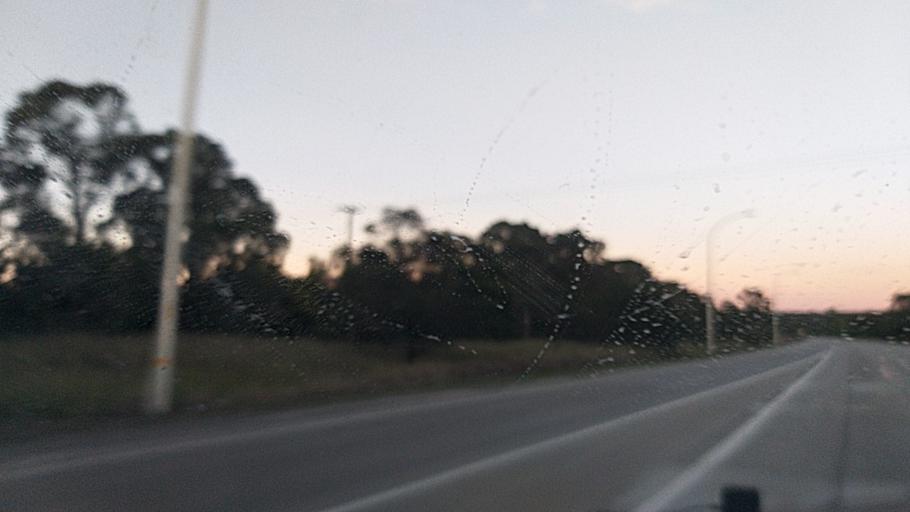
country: AU
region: New South Wales
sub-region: Goulburn Mulwaree
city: Goulburn
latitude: -34.7193
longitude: 149.9975
